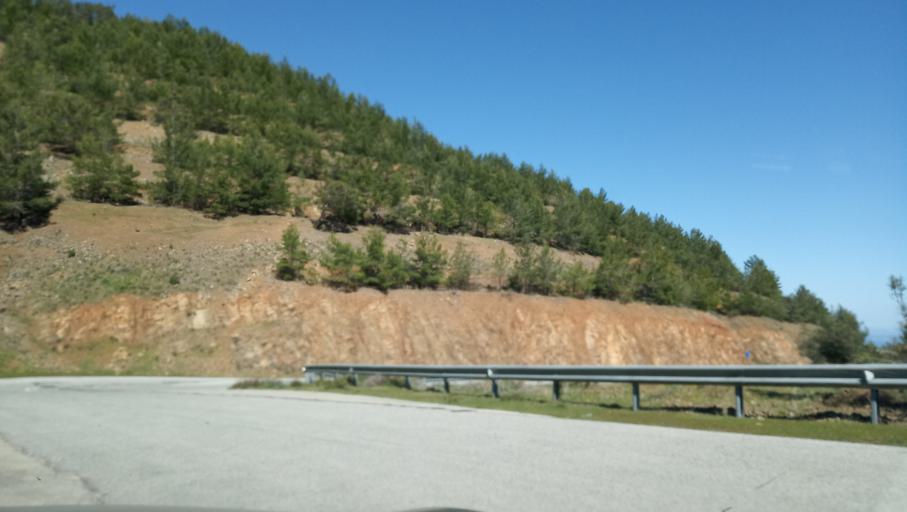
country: CY
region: Lefkosia
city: Lefka
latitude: 35.0826
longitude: 32.7801
